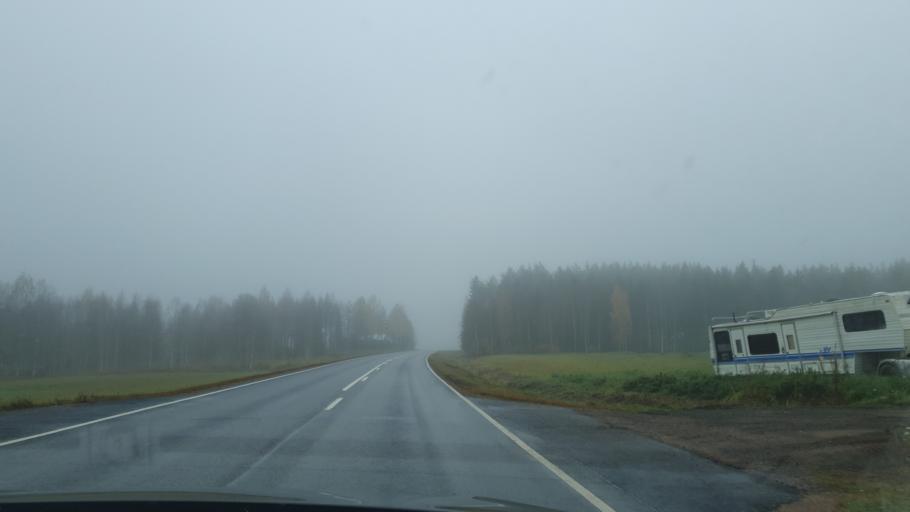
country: FI
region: Lapland
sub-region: Rovaniemi
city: Rovaniemi
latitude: 66.8057
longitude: 25.4123
